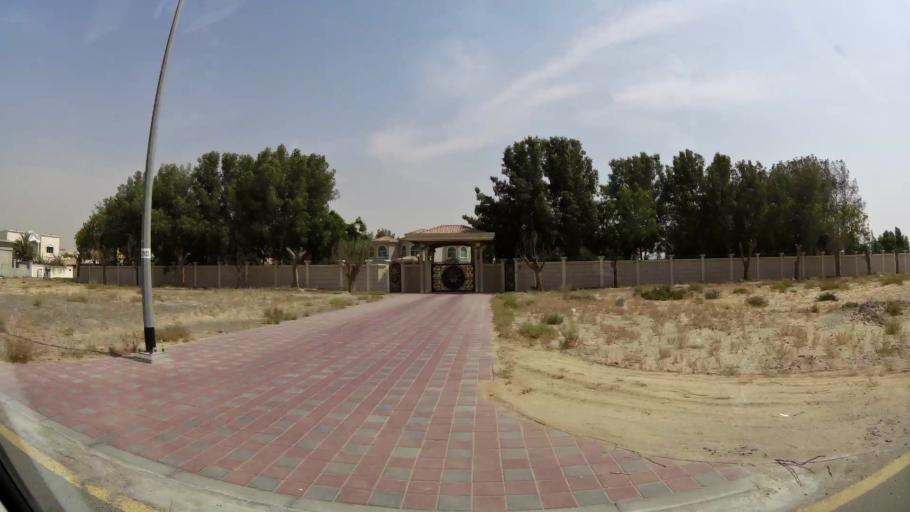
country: AE
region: Ash Shariqah
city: Sharjah
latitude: 25.2520
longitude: 55.4805
